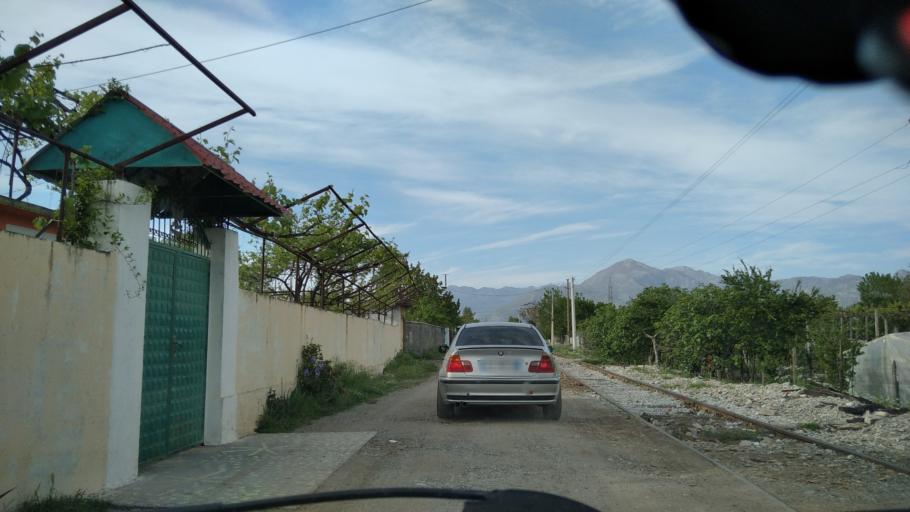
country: AL
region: Shkoder
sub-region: Rrethi i Shkodres
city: Shkoder
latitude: 42.0687
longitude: 19.5286
